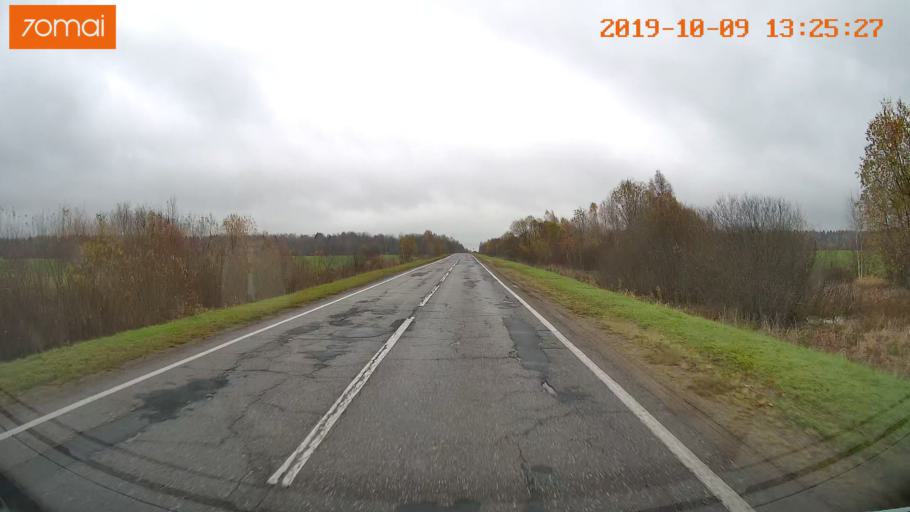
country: RU
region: Jaroslavl
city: Lyubim
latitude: 58.3283
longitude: 40.9110
